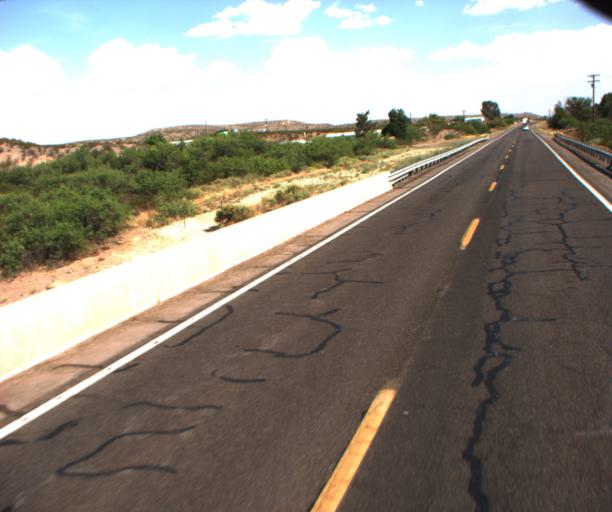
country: US
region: Arizona
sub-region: Greenlee County
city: Clifton
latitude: 32.8257
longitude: -109.1747
